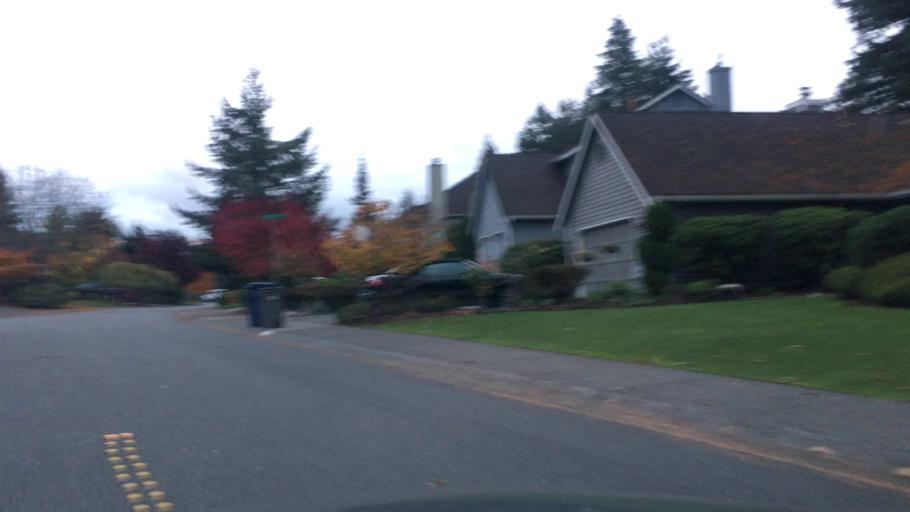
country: US
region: Washington
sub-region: Snohomish County
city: Mill Creek
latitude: 47.8522
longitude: -122.1991
